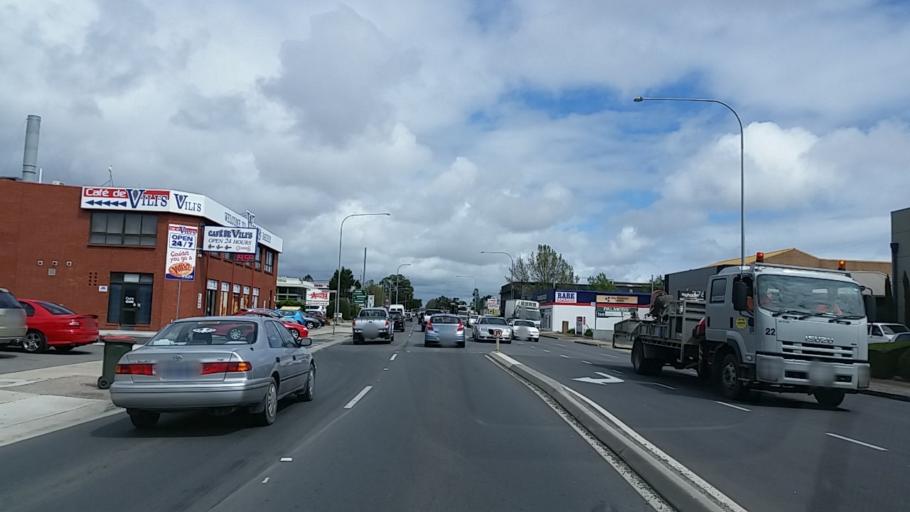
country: AU
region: South Australia
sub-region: Unley
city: Forestville
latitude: -34.9390
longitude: 138.5709
